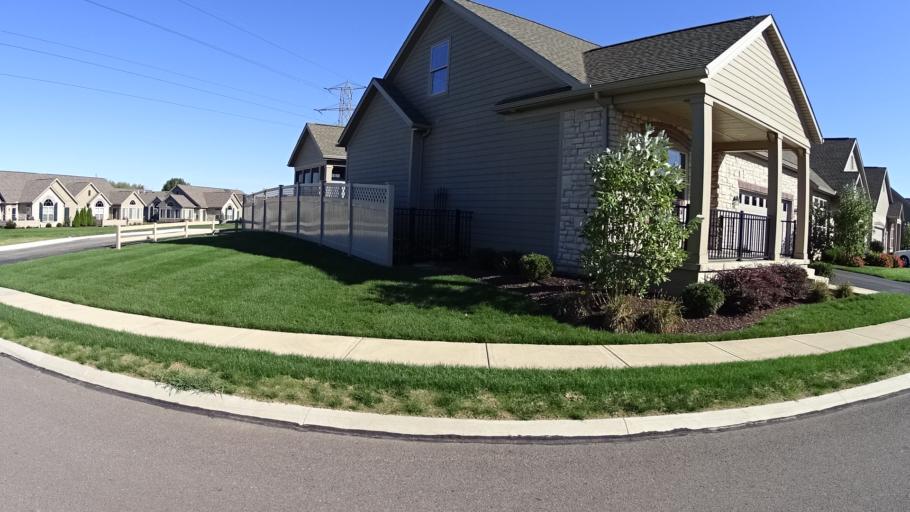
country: US
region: Ohio
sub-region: Lorain County
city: Amherst
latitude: 41.4158
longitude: -82.2207
